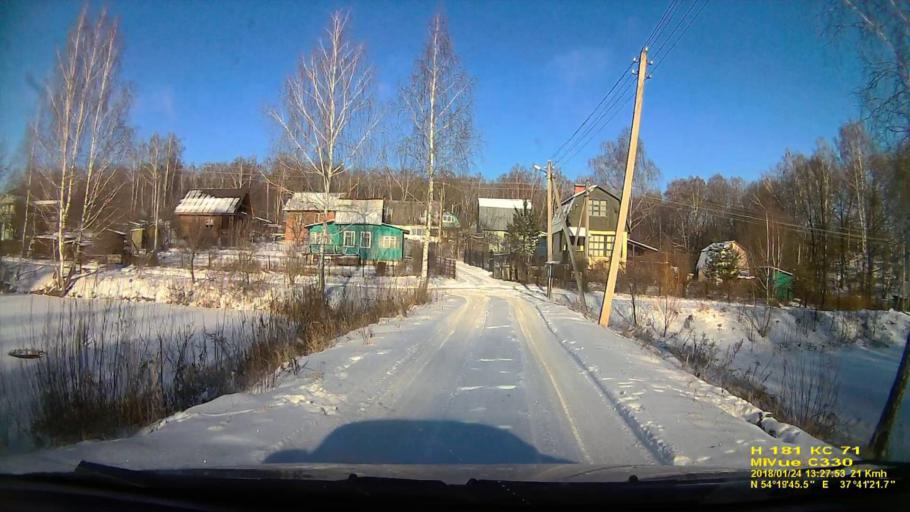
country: RU
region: Tula
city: Revyakino
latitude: 54.3295
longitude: 37.6896
